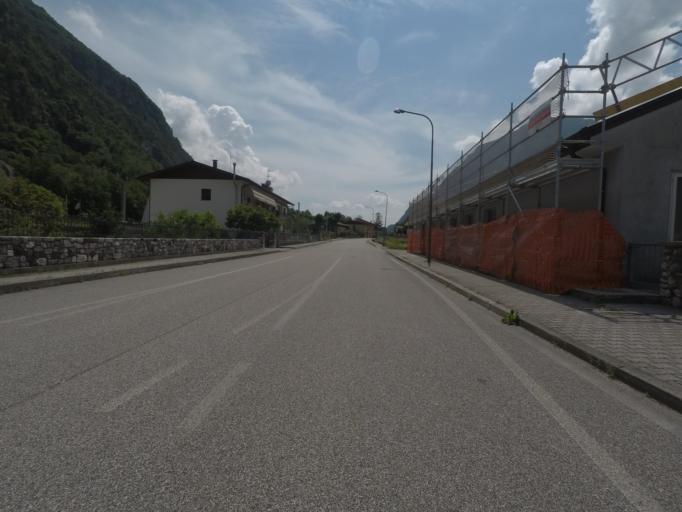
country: IT
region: Friuli Venezia Giulia
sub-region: Provincia di Udine
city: Amaro
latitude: 46.3725
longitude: 13.1346
